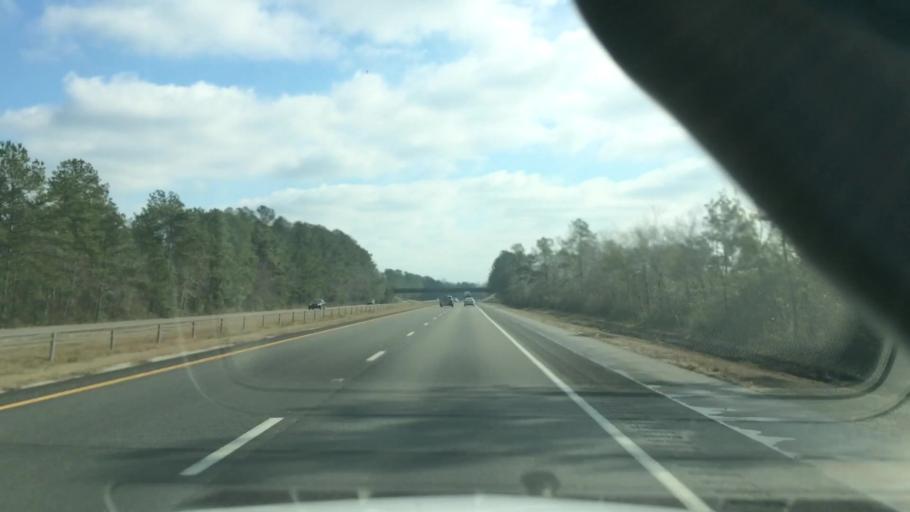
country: US
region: North Carolina
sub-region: Pender County
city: Burgaw
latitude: 34.6153
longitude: -77.9241
